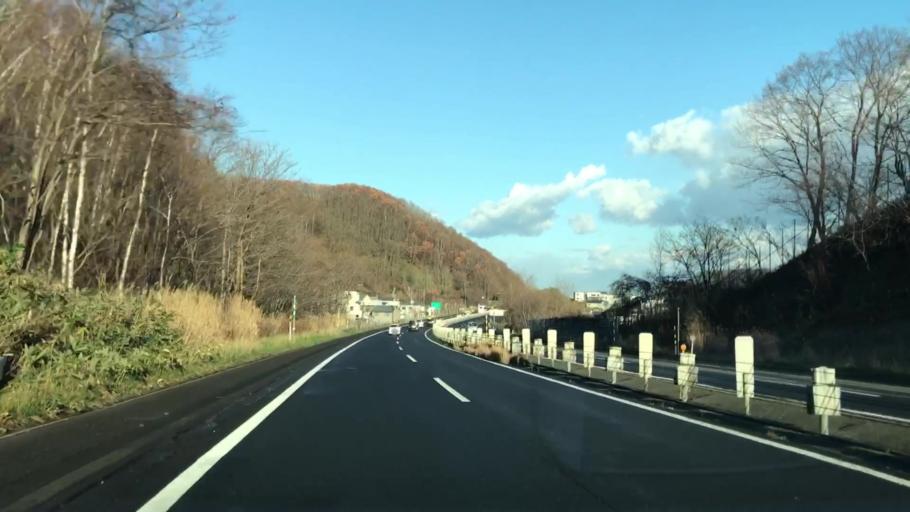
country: JP
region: Hokkaido
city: Sapporo
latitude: 43.1031
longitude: 141.2449
